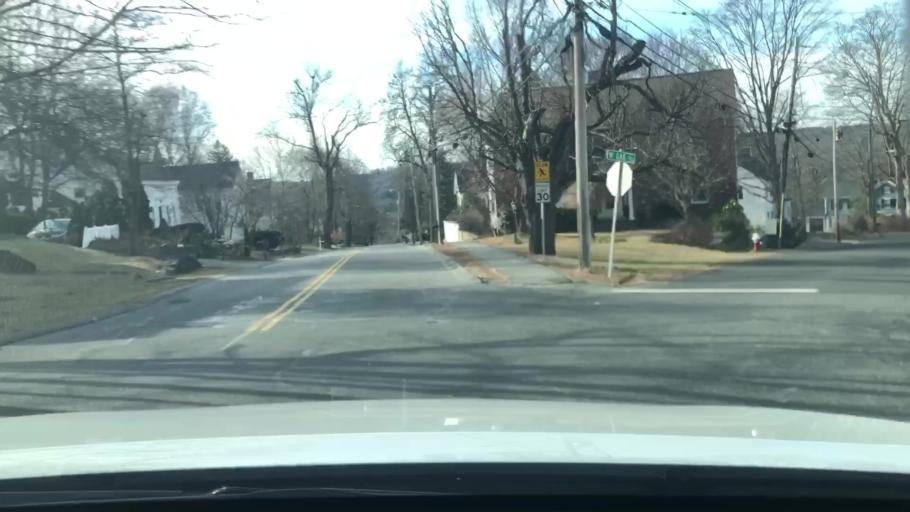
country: US
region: Massachusetts
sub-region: Worcester County
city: Grafton
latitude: 42.2067
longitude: -71.6866
